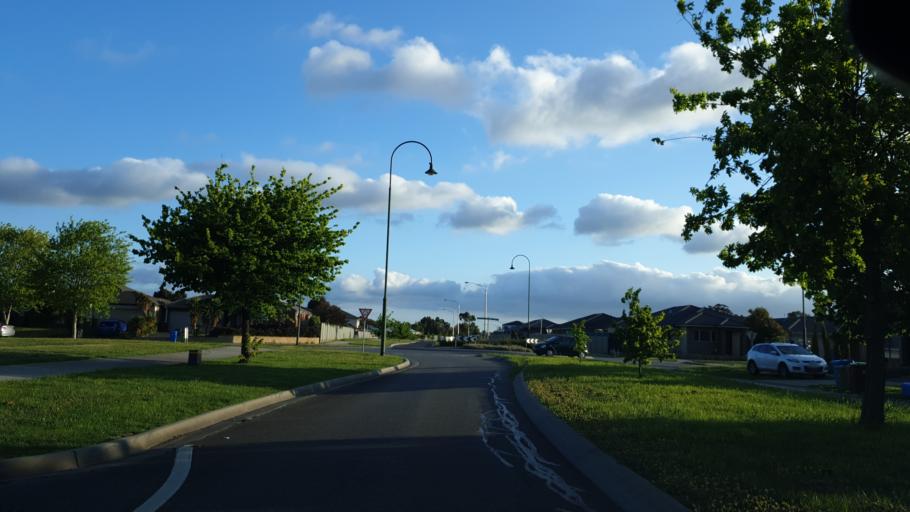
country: AU
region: Victoria
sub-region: Casey
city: Cranbourne East
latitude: -38.1083
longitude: 145.3009
